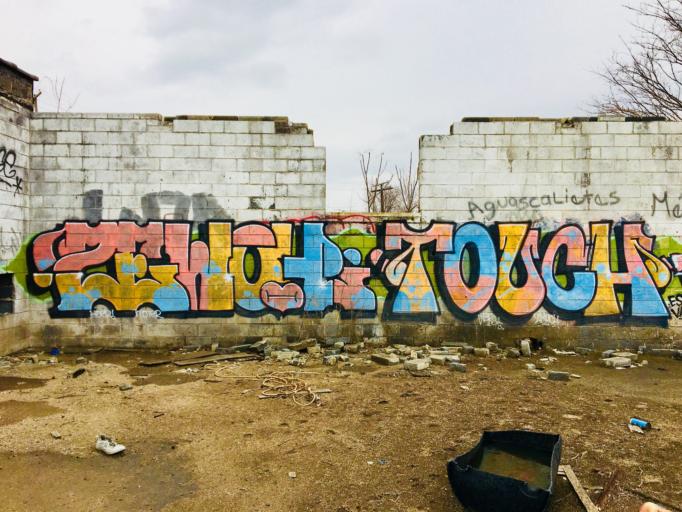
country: US
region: Michigan
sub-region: Wayne County
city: River Rouge
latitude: 42.2910
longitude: -83.1194
